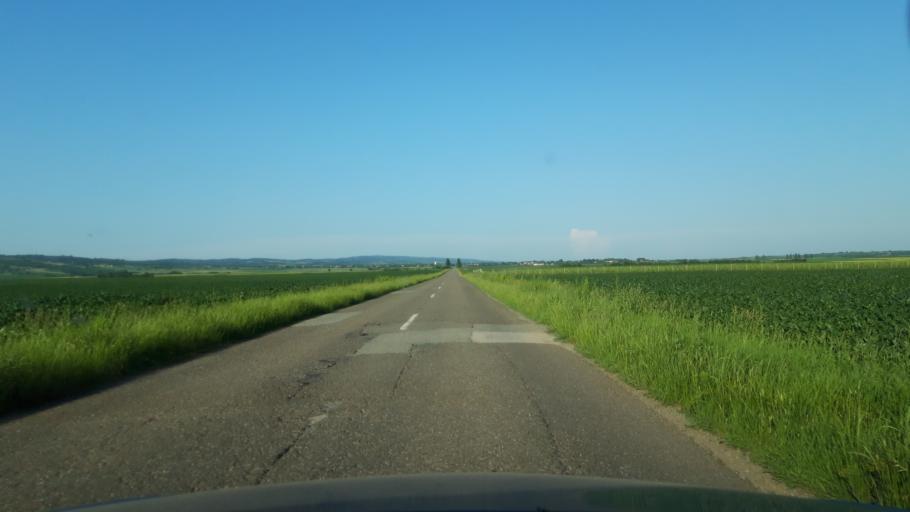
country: HR
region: Vukovarsko-Srijemska
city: Ilok
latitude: 45.1026
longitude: 19.4646
